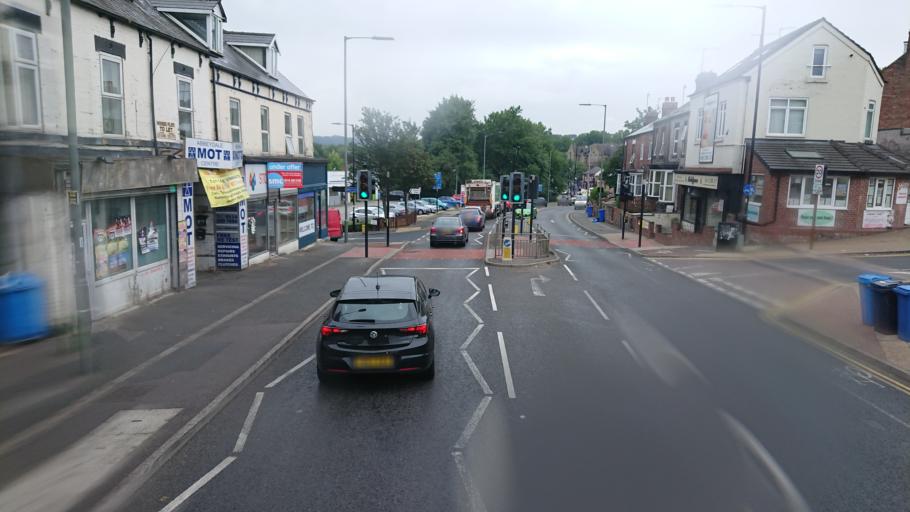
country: GB
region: England
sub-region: Sheffield
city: Sheffield
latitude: 53.3595
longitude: -1.4803
